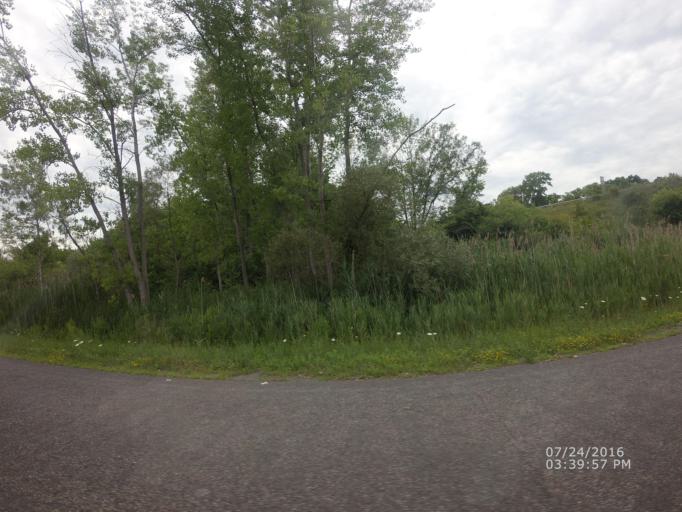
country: US
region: New York
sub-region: Onondaga County
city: Camillus
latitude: 43.0480
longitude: -76.3048
